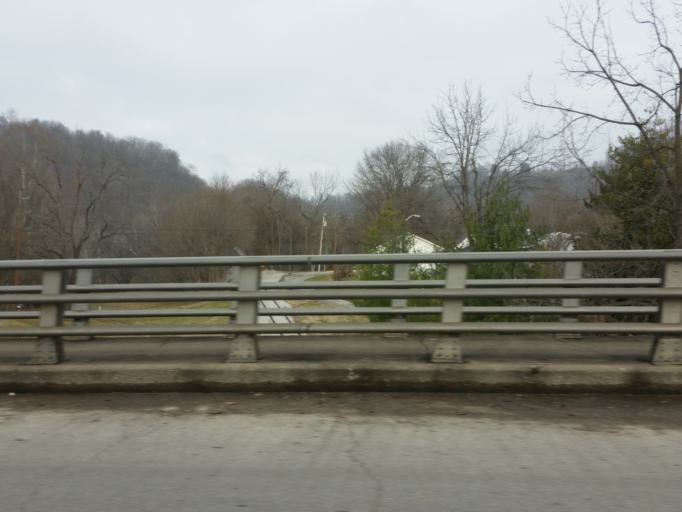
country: US
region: Indiana
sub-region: Jefferson County
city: Madison
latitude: 38.7393
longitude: -85.3962
